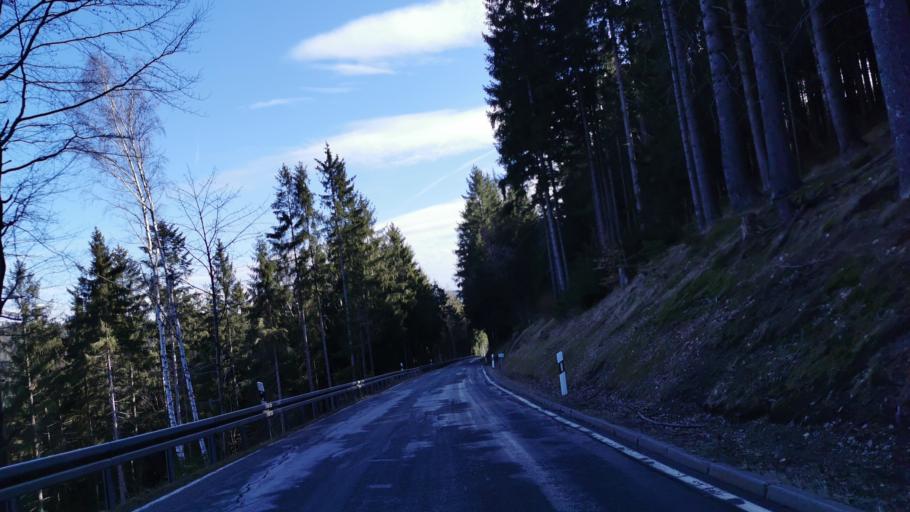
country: DE
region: Thuringia
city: Grafenthal
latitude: 50.4860
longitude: 11.3064
